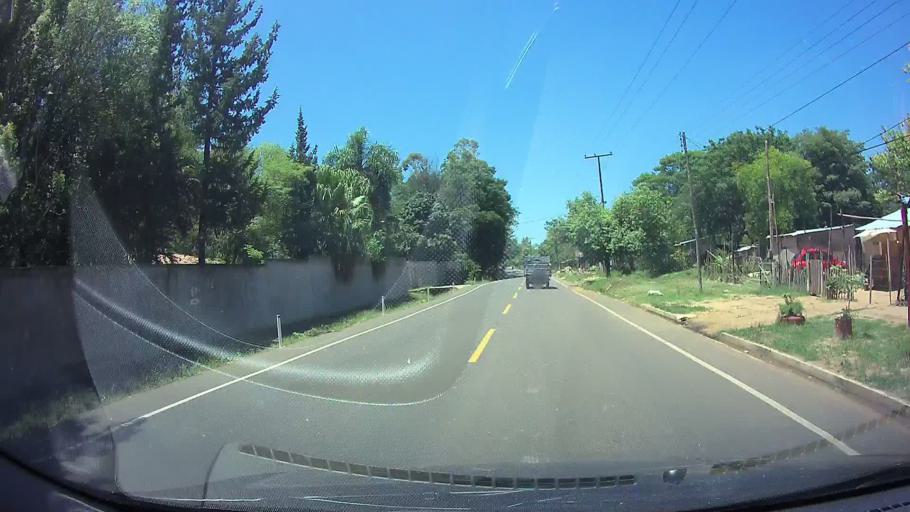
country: PY
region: Central
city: Limpio
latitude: -25.2433
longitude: -57.4912
